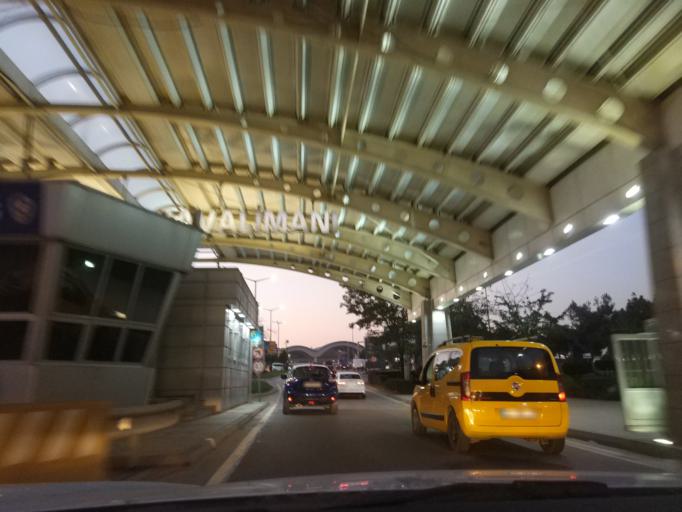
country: TR
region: Istanbul
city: Pendik
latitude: 40.9121
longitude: 29.3134
